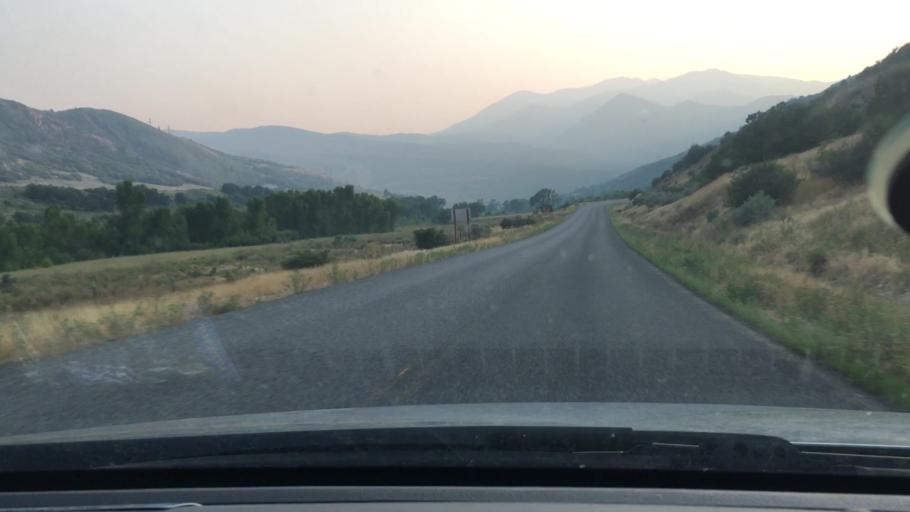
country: US
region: Utah
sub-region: Utah County
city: Mapleton
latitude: 40.0421
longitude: -111.4819
